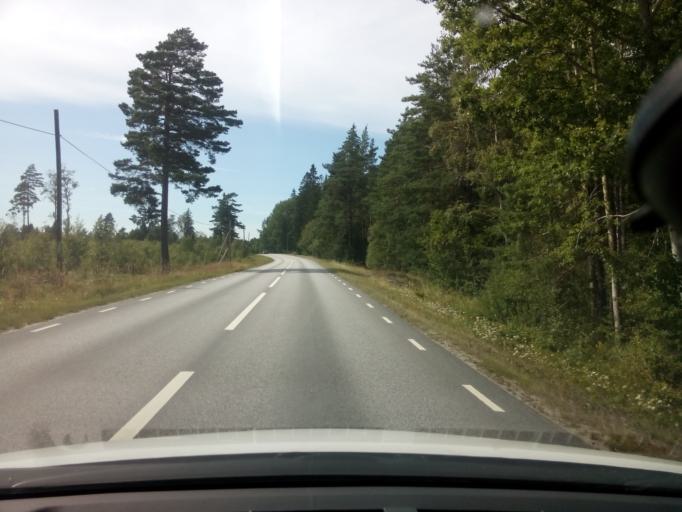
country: SE
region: Soedermanland
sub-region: Oxelosunds Kommun
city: Oxelosund
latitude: 58.7410
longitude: 17.1733
